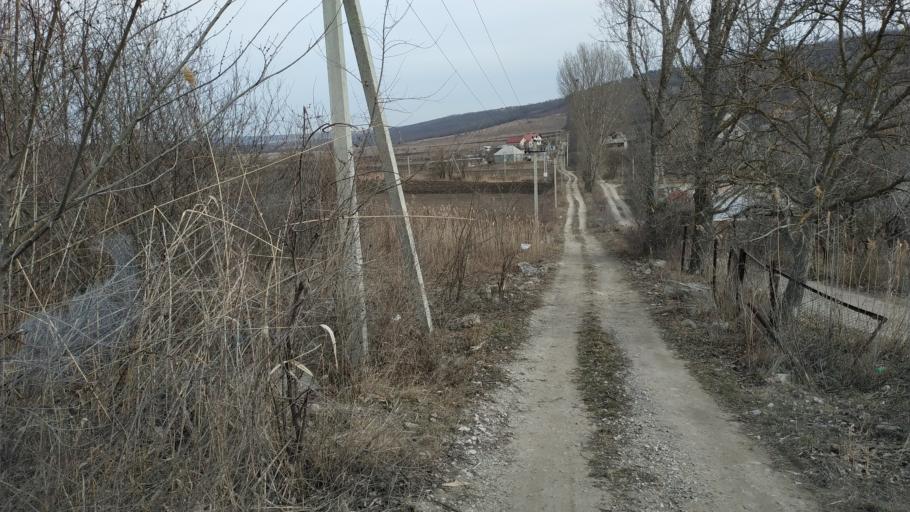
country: MD
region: Chisinau
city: Vatra
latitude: 47.0965
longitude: 28.7347
